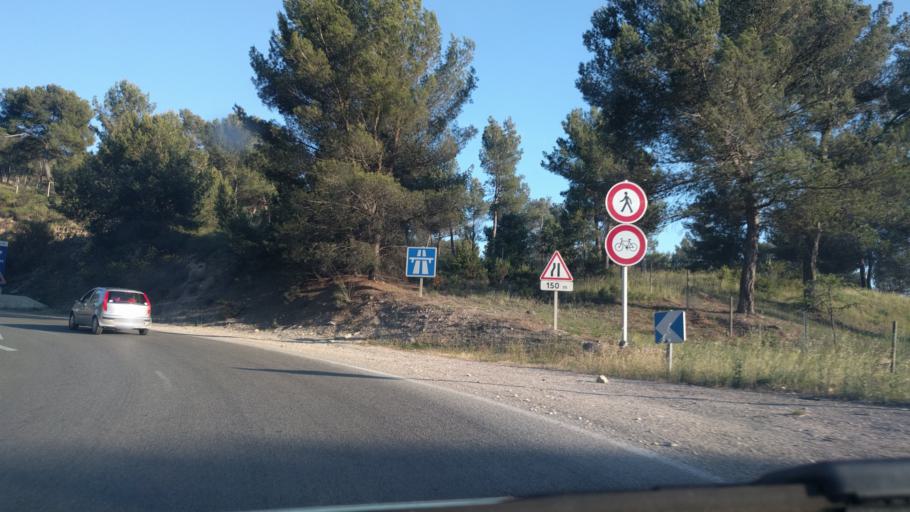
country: FR
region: Provence-Alpes-Cote d'Azur
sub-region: Departement des Bouches-du-Rhone
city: Venelles
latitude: 43.6073
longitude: 5.4948
